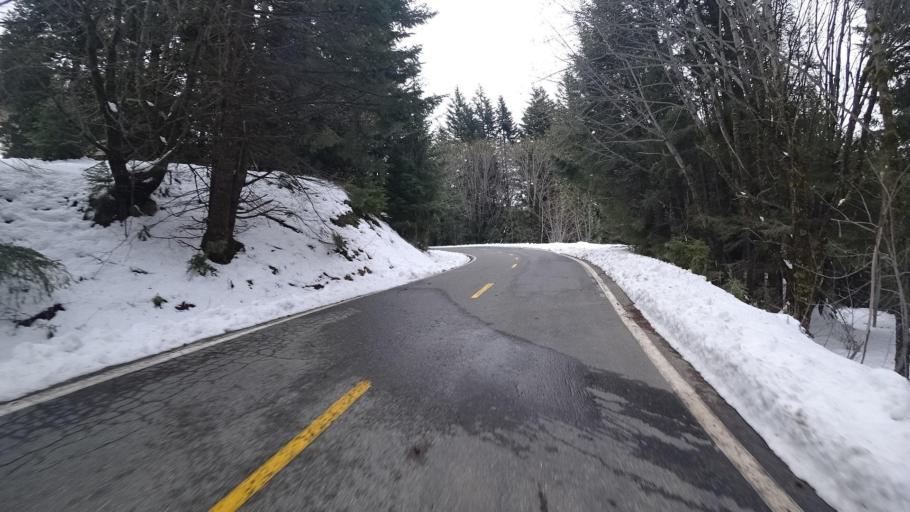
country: US
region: California
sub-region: Humboldt County
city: Willow Creek
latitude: 40.8683
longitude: -123.7461
